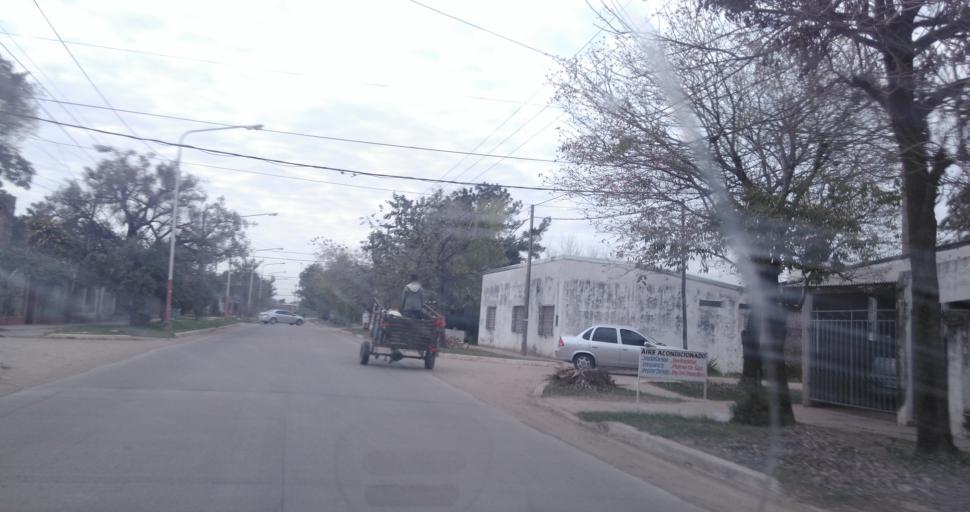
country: AR
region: Chaco
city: Fontana
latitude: -27.4529
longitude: -59.0345
